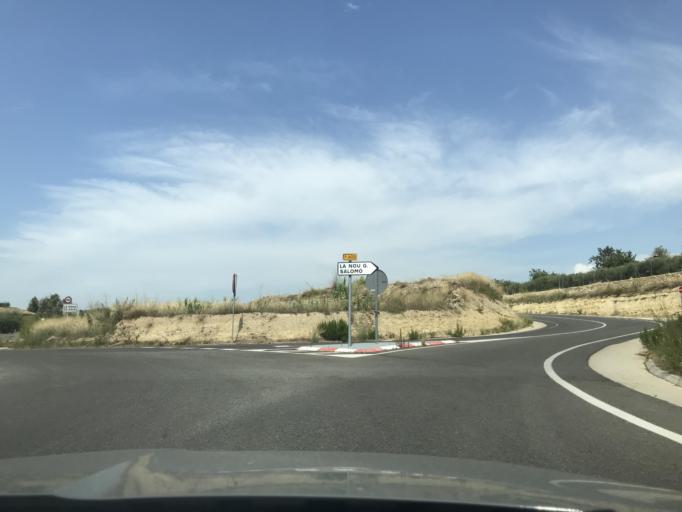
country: ES
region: Catalonia
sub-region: Provincia de Tarragona
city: Altafulla
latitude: 41.1677
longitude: 1.3671
